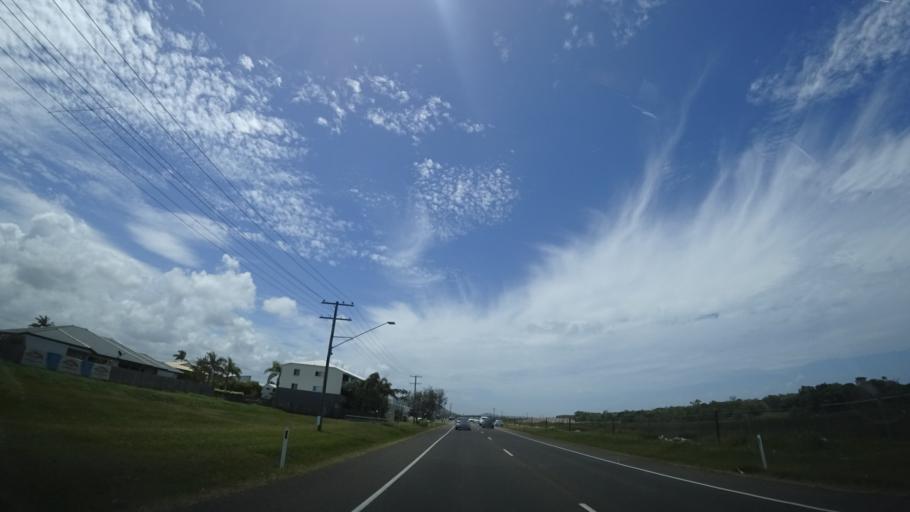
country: AU
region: Queensland
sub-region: Sunshine Coast
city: Coolum Beach
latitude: -26.5995
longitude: 153.0958
